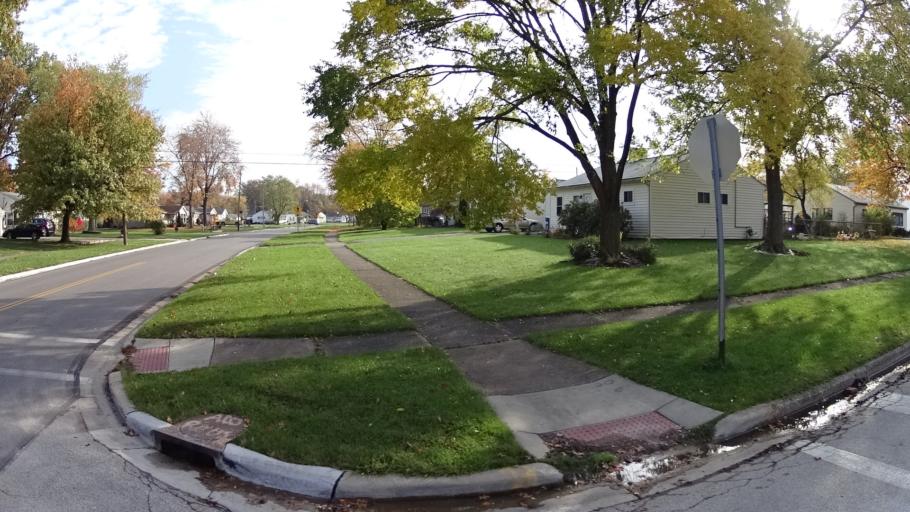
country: US
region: Ohio
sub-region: Lorain County
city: Sheffield
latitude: 41.4305
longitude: -82.1087
